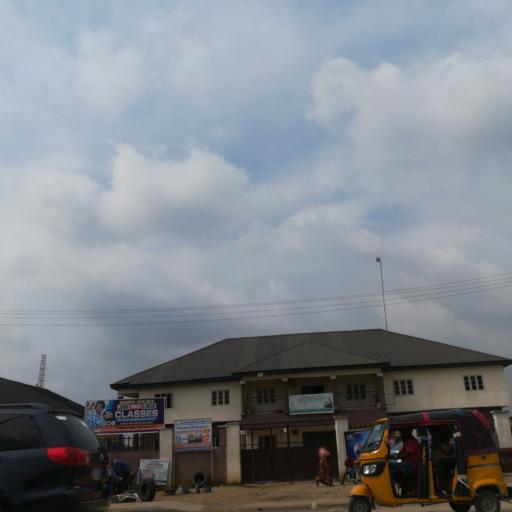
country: NG
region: Rivers
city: Port Harcourt
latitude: 4.8406
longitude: 7.0685
